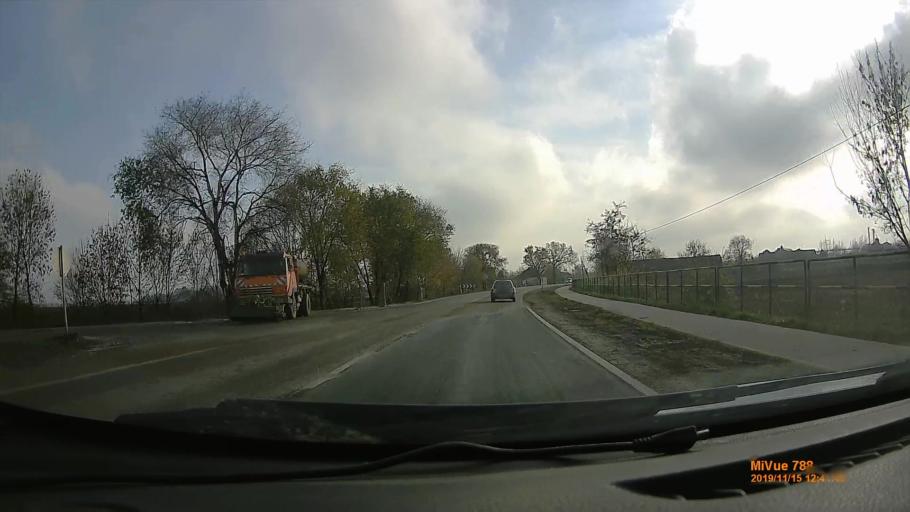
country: HU
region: Bekes
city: Bekescsaba
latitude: 46.7035
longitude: 21.0123
